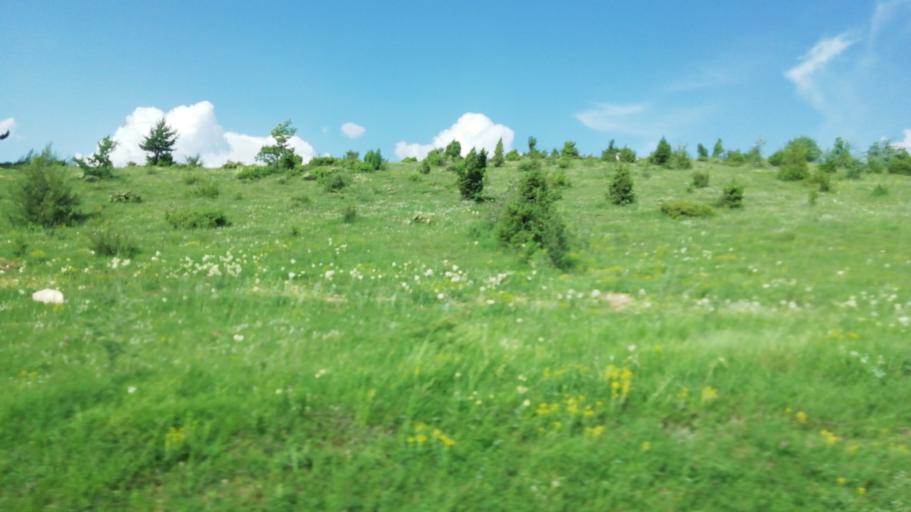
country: TR
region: Karabuk
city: Karabuk
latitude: 41.1248
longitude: 32.5805
